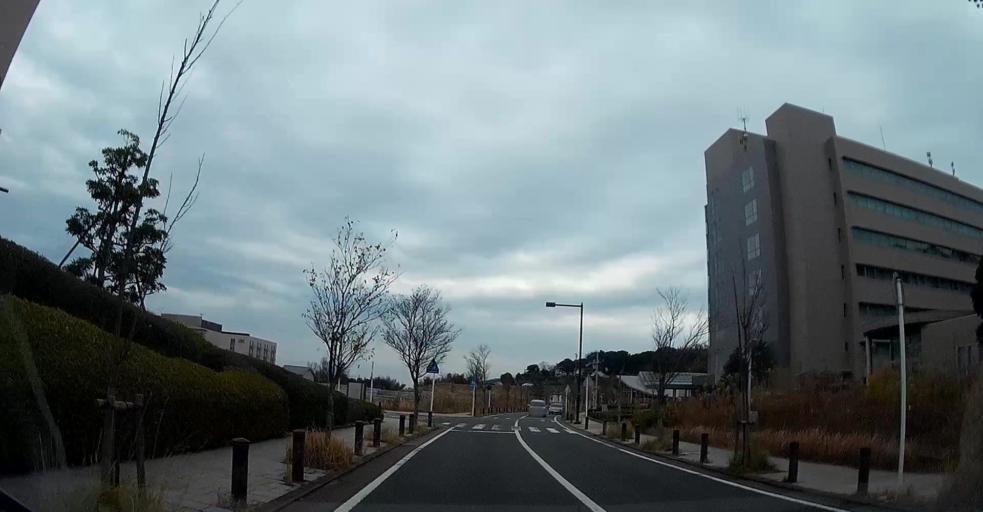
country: JP
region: Kanagawa
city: Yokosuka
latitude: 35.2244
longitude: 139.6756
